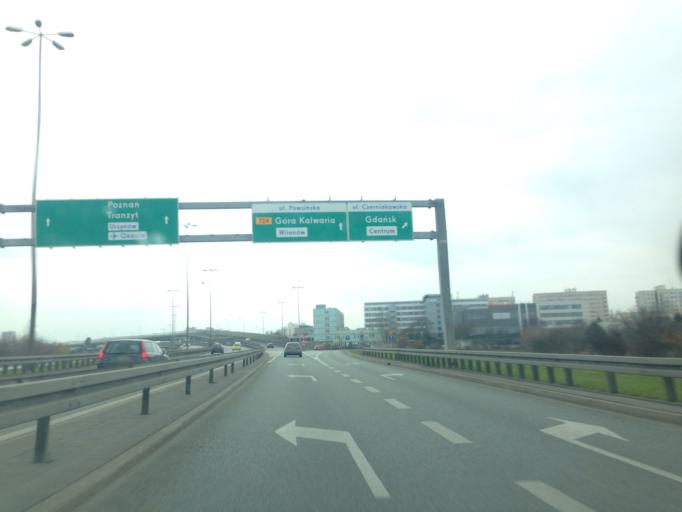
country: PL
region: Masovian Voivodeship
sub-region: Warszawa
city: Mokotow
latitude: 52.2013
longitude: 21.0581
